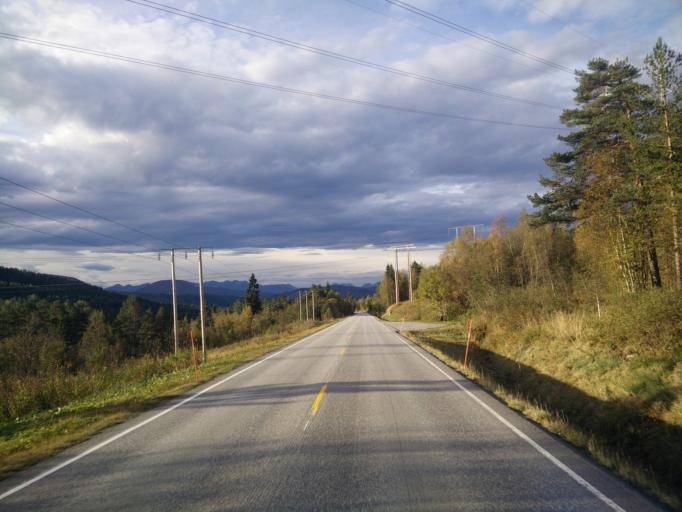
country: NO
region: More og Romsdal
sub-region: Molde
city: Hjelset
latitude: 62.8114
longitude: 7.5897
